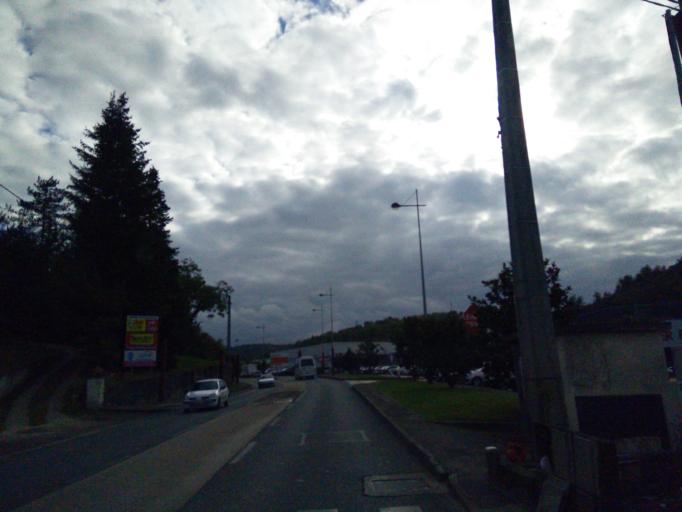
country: FR
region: Midi-Pyrenees
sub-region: Departement du Lot
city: Cahors
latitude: 44.4232
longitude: 1.4397
